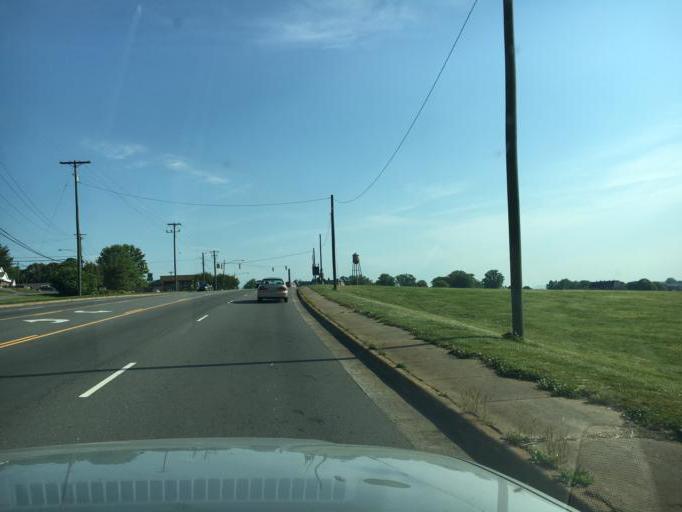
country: US
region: North Carolina
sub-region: Burke County
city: Morganton
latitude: 35.7232
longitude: -81.6933
